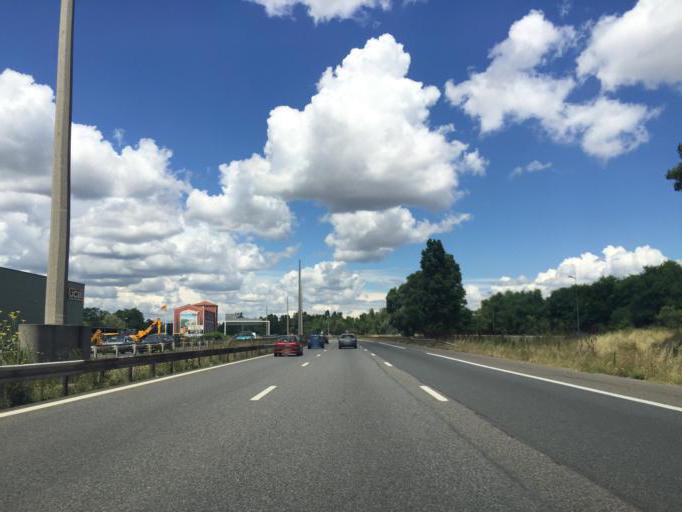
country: FR
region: Rhone-Alpes
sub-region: Departement du Rhone
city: Pierre-Benite
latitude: 45.7012
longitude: 4.8355
